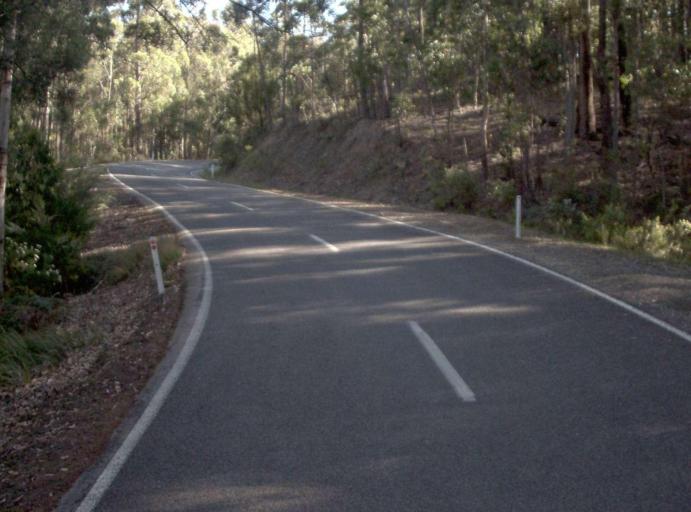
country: AU
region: Victoria
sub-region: East Gippsland
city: Lakes Entrance
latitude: -37.6346
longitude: 148.4813
